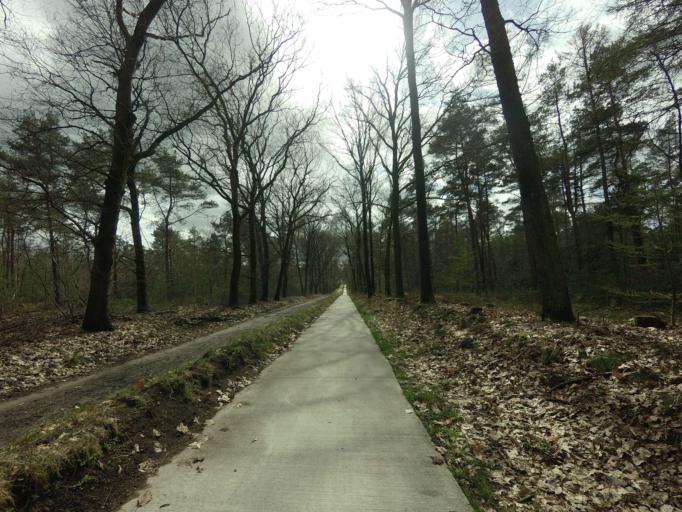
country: NL
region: Gelderland
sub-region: Gemeente Renkum
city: Heelsum
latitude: 52.0111
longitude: 5.7518
